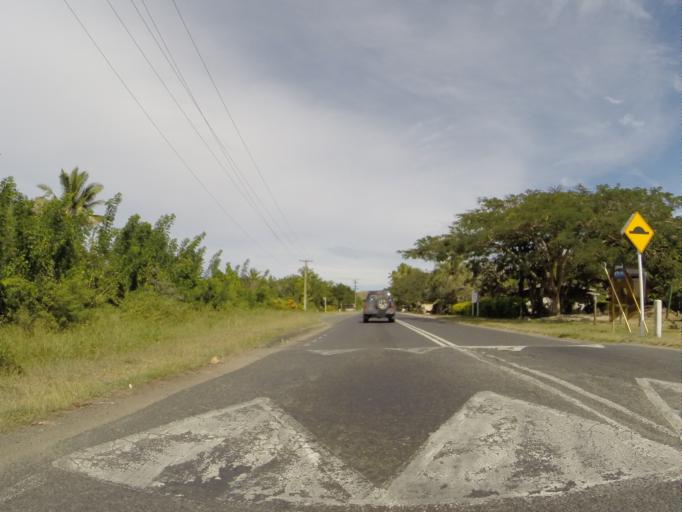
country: FJ
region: Western
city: Nadi
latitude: -18.1577
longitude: 177.4909
